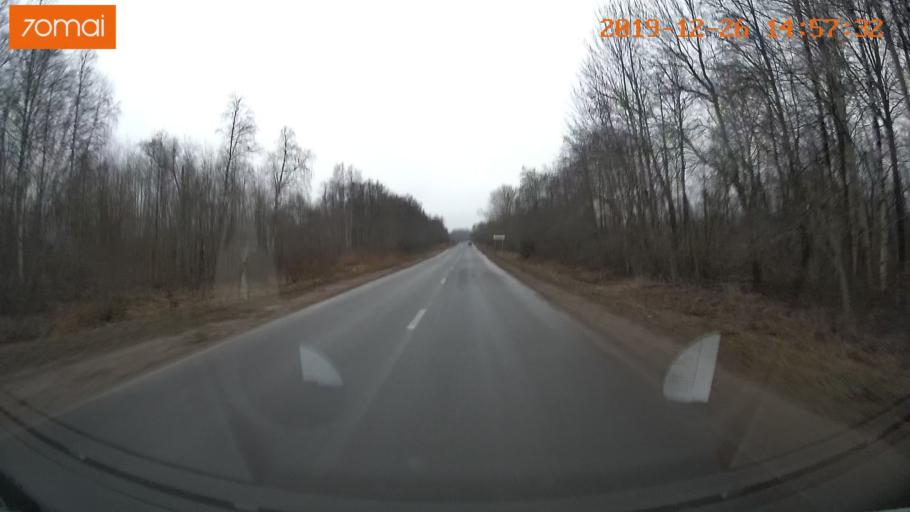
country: RU
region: Jaroslavl
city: Rybinsk
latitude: 58.2816
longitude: 38.8621
